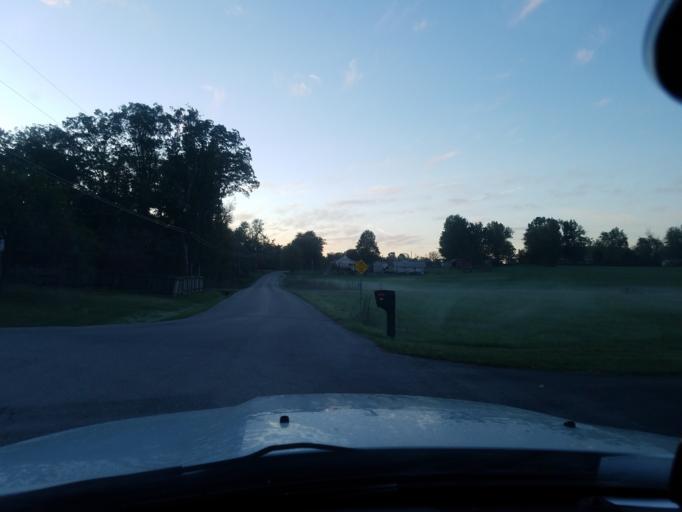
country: US
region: Kentucky
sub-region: Laurel County
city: London
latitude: 37.0957
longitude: -84.0796
